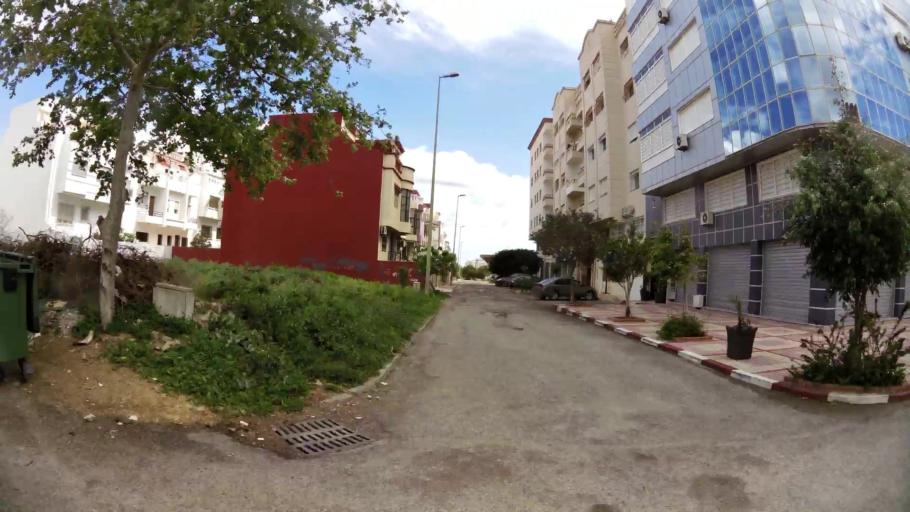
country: MA
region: Tanger-Tetouan
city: Tetouan
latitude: 35.5906
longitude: -5.3418
